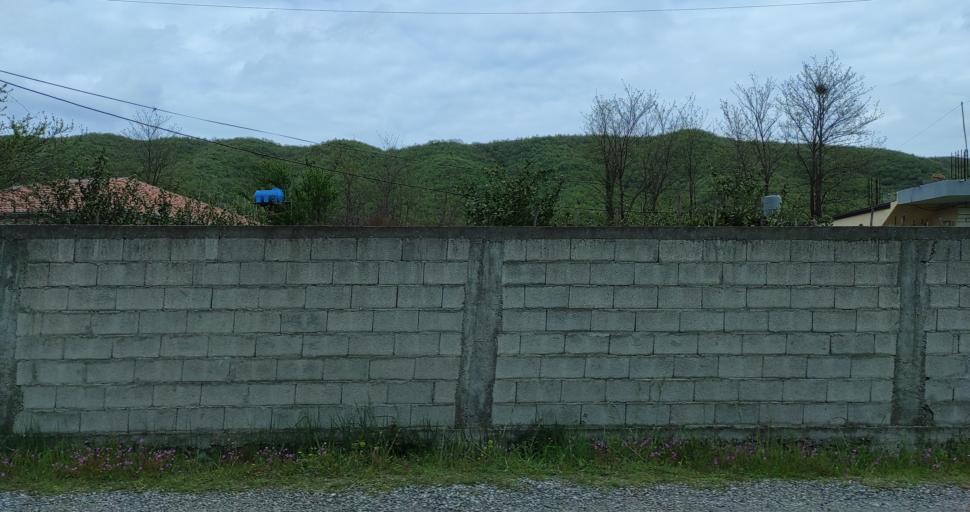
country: AL
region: Shkoder
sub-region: Rrethi i Shkodres
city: Dajc
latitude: 42.0202
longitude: 19.3819
